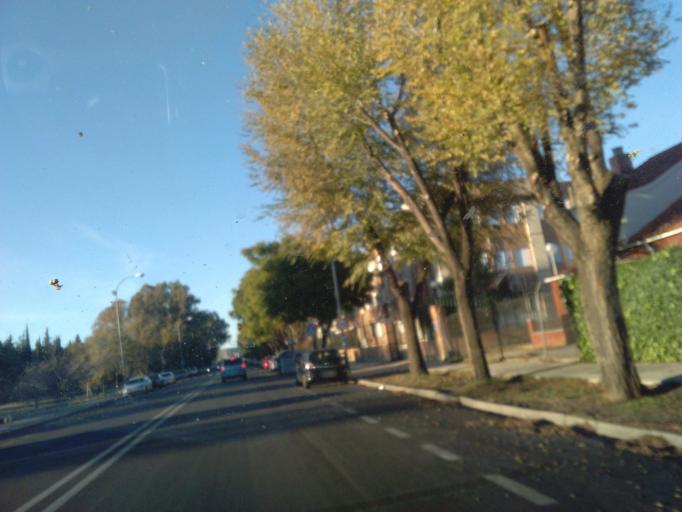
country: ES
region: Andalusia
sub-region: Provincia de Sevilla
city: Sevilla
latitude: 37.3974
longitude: -5.9302
